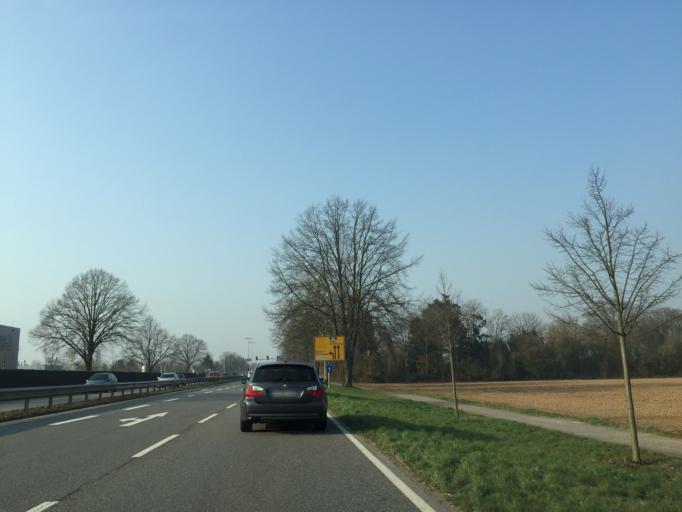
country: DE
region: Baden-Wuerttemberg
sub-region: Karlsruhe Region
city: Eppelheim
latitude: 49.3853
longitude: 8.6574
